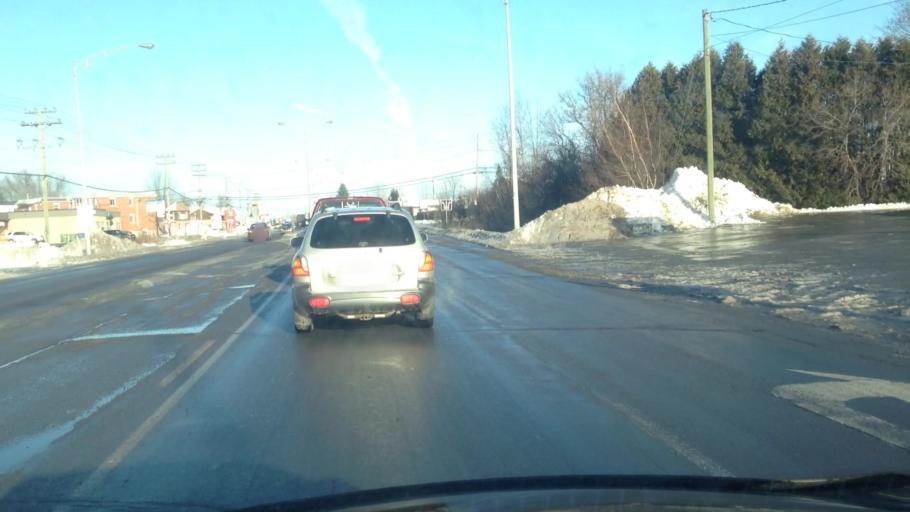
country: CA
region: Quebec
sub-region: Laurentides
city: Saint-Jerome
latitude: 45.7652
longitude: -73.9803
